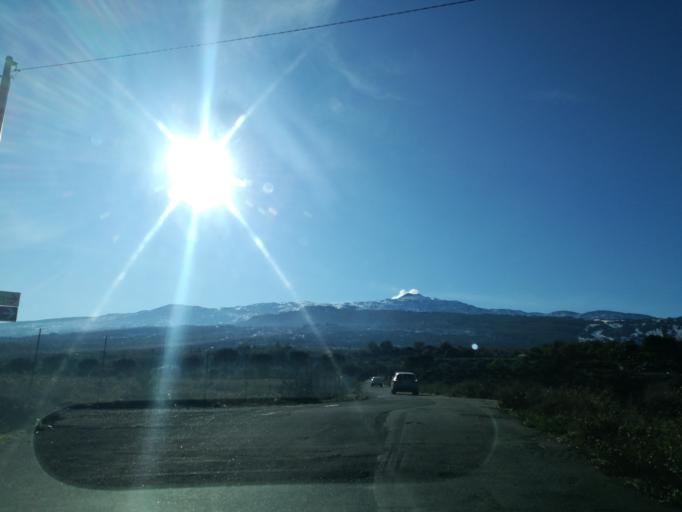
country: IT
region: Sicily
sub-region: Catania
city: Randazzo
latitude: 37.8665
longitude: 14.9798
